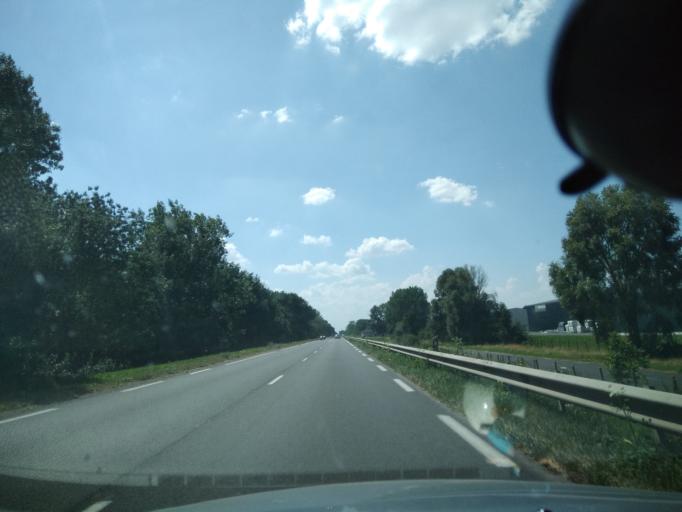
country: FR
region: Centre
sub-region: Departement d'Indre-et-Loire
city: La Ville-aux-Dames
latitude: 47.3812
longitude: 0.7698
